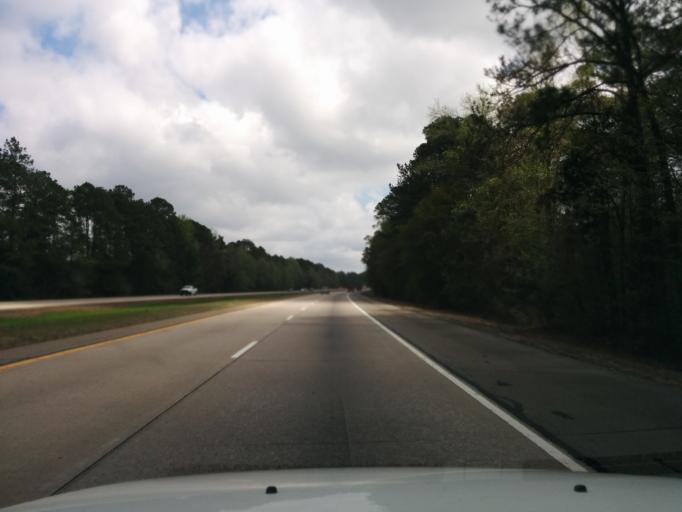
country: US
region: Georgia
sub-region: Bryan County
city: Pembroke
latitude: 32.2102
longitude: -81.5009
